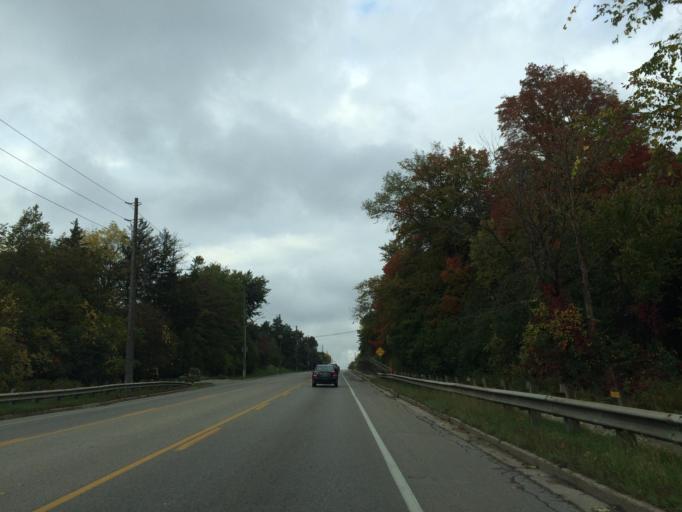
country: CA
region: Ontario
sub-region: Wellington County
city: Guelph
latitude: 43.5700
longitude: -80.2705
